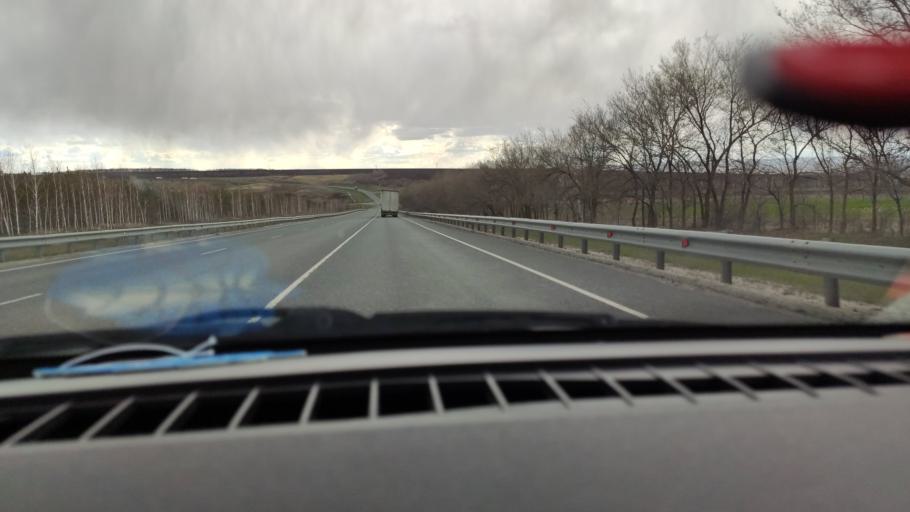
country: RU
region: Saratov
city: Balakovo
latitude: 52.1306
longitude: 47.7635
